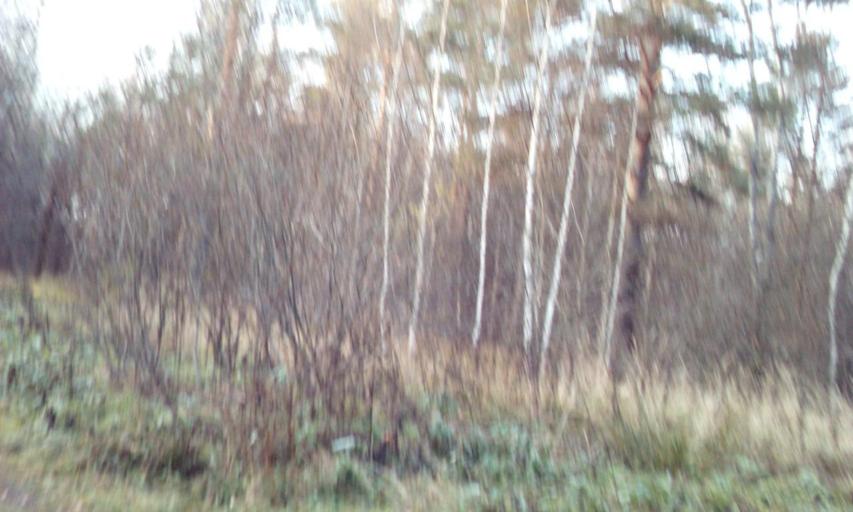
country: RU
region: Moskovskaya
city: Aprelevka
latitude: 55.5553
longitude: 37.1005
